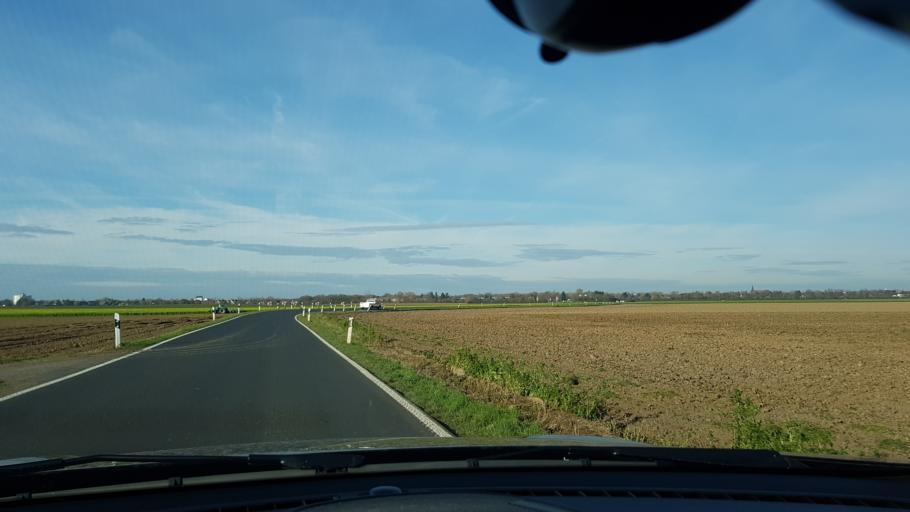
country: DE
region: North Rhine-Westphalia
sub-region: Regierungsbezirk Dusseldorf
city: Neubrueck
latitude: 51.0951
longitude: 6.6378
